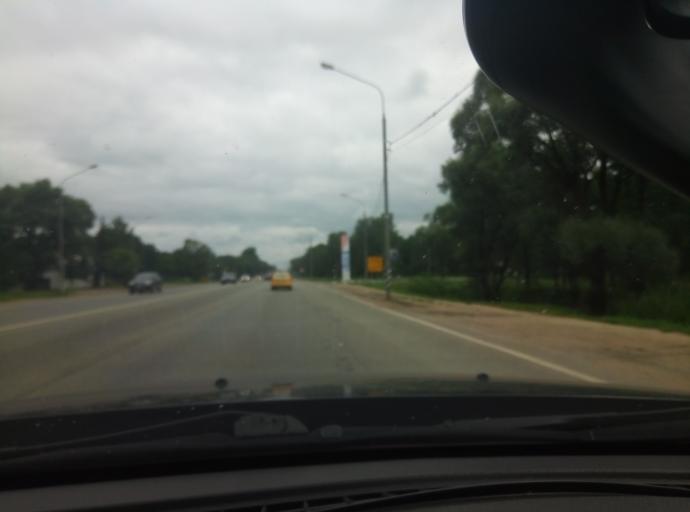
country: RU
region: Kaluga
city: Obninsk
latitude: 55.0945
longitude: 36.6365
